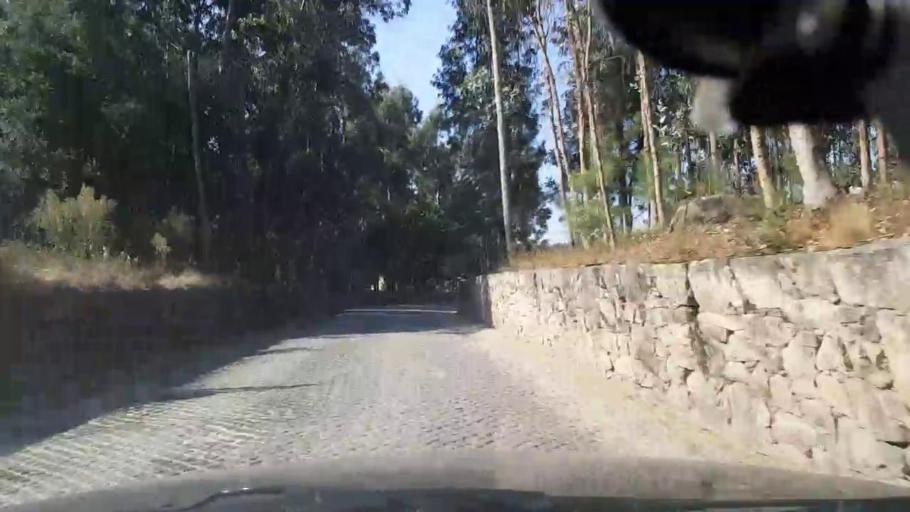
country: PT
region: Porto
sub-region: Vila do Conde
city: Arvore
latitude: 41.3838
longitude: -8.6849
